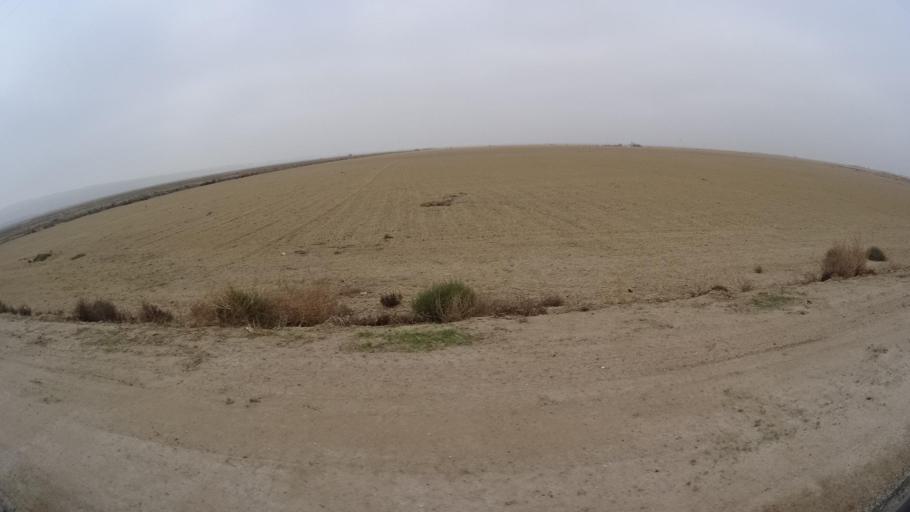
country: US
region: California
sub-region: Kern County
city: Maricopa
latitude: 35.1229
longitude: -119.3220
